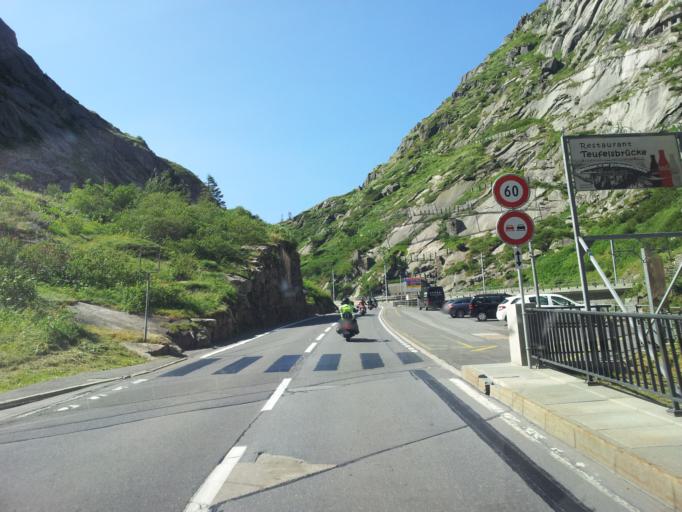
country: CH
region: Uri
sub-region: Uri
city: Andermatt
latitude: 46.6478
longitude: 8.5908
